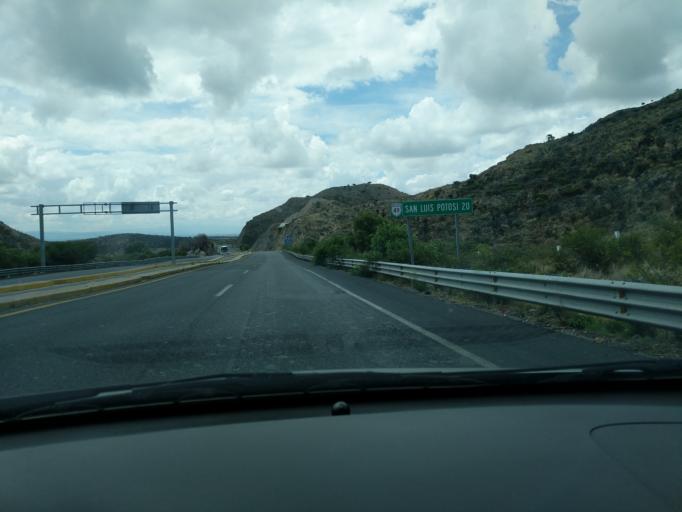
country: MX
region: San Luis Potosi
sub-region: Mexquitic de Carmona
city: Cerrito de Jaral
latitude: 22.2493
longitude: -101.1055
